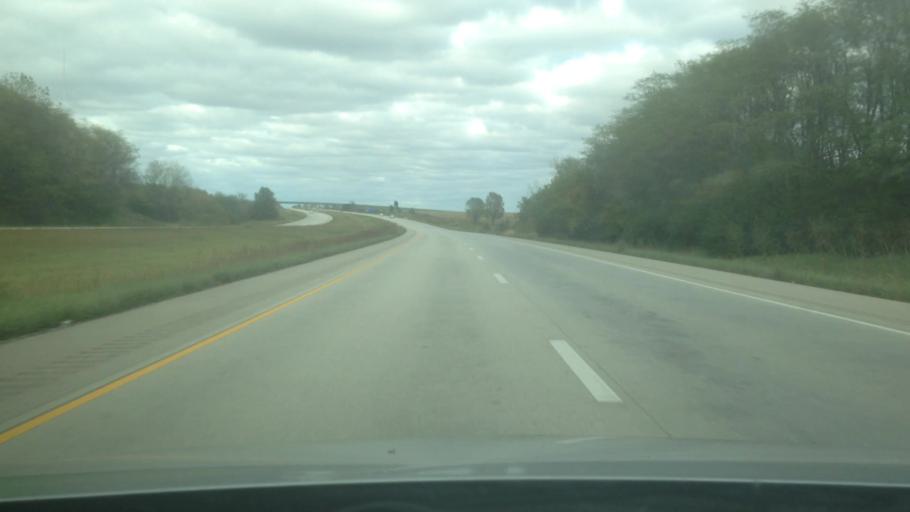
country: US
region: Illinois
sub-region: Macon County
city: Forsyth
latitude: 39.9299
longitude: -88.8443
